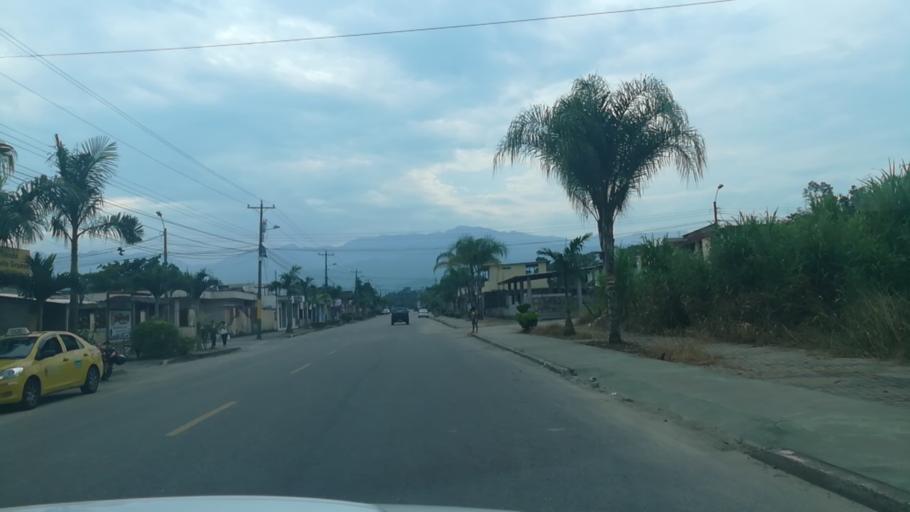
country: EC
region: Napo
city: Tena
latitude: -0.9847
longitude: -77.8207
